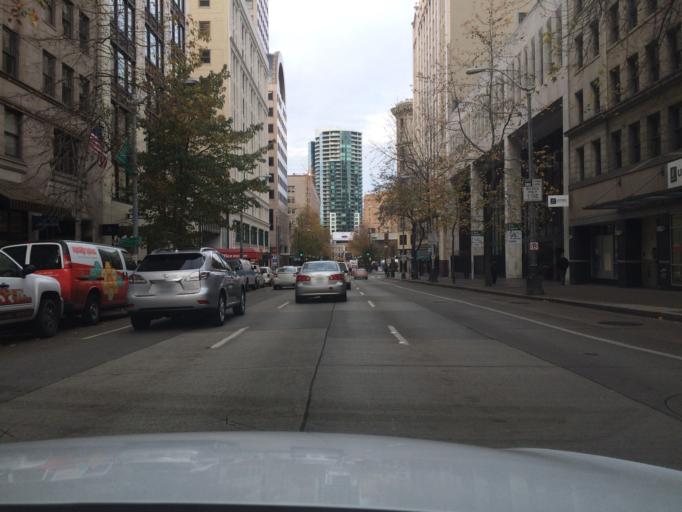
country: US
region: Washington
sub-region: King County
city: Seattle
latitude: 47.6092
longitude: -122.3358
